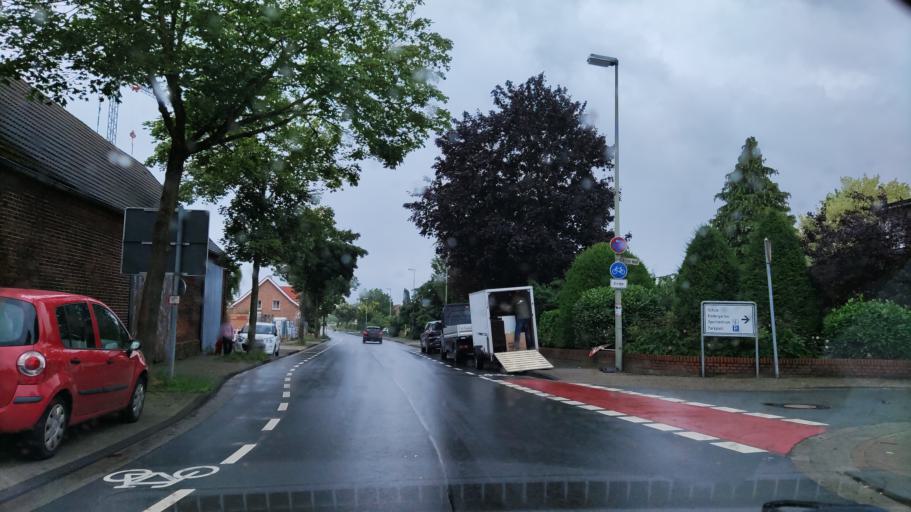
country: DE
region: North Rhine-Westphalia
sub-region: Regierungsbezirk Munster
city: Everswinkel
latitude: 51.9123
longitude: 7.8104
